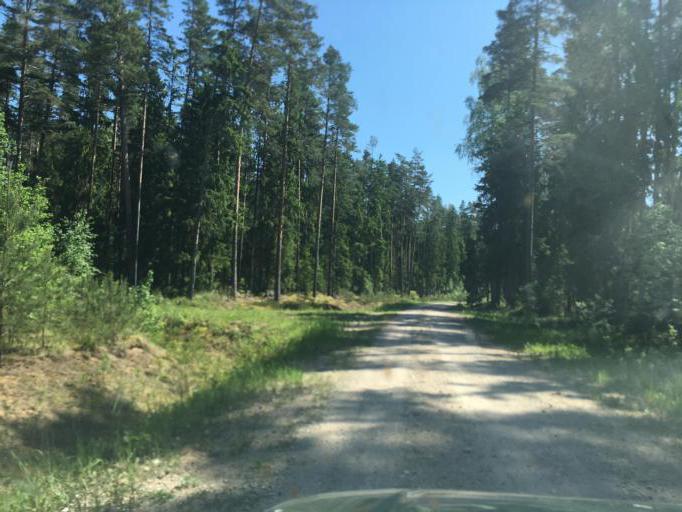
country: LV
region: Talsu Rajons
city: Valdemarpils
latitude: 57.4437
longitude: 22.6629
